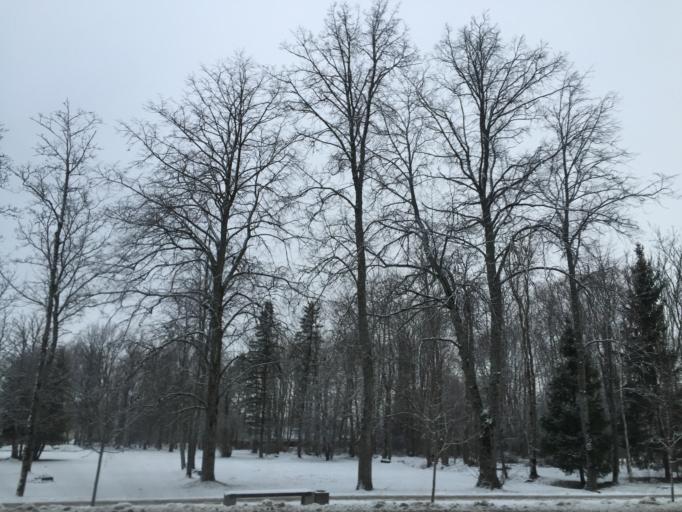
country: EE
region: Laeaene
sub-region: Lihula vald
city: Lihula
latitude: 58.6860
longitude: 23.8327
